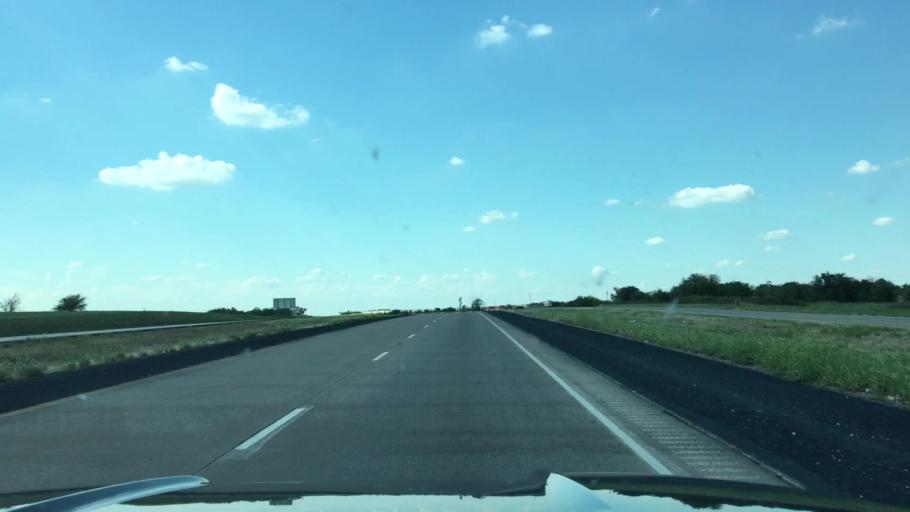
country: US
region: Texas
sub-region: Wise County
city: New Fairview
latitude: 33.1165
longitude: -97.4811
